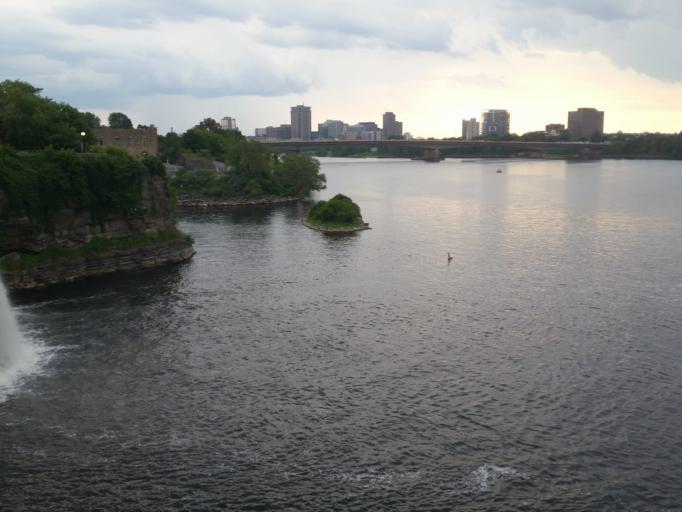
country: CA
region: Ontario
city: Ottawa
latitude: 45.4418
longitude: -75.6959
